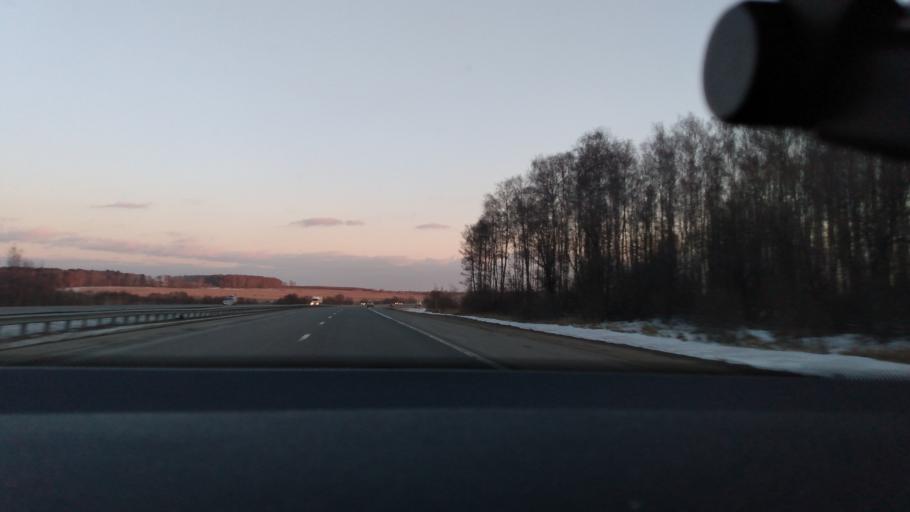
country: RU
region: Moskovskaya
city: Kolomna
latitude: 55.1075
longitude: 38.8847
